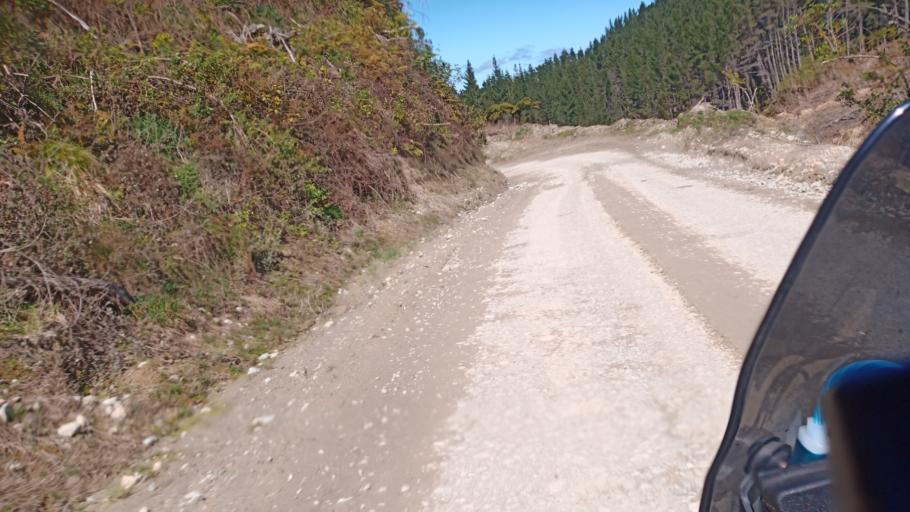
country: NZ
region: Gisborne
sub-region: Gisborne District
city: Gisborne
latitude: -38.8842
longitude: 177.7833
